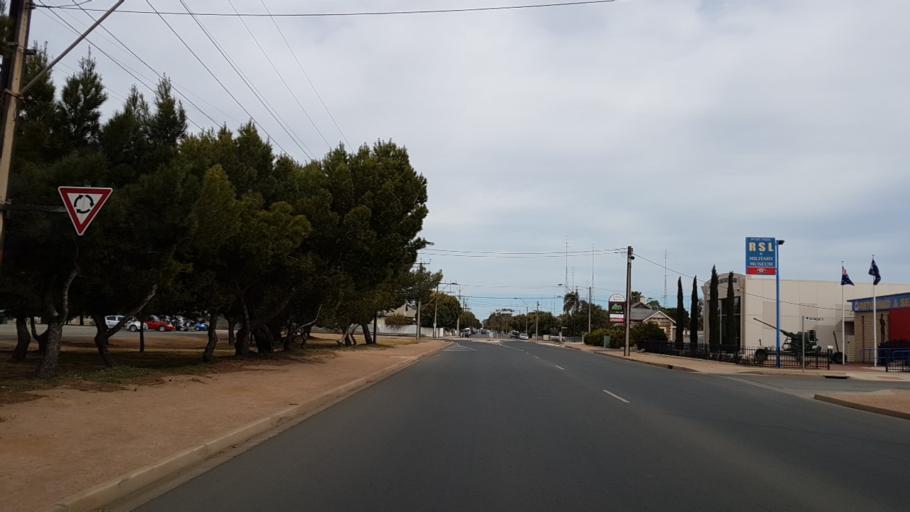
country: AU
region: South Australia
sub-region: Port Pirie City and Dists
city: Port Pirie
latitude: -33.1884
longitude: 138.0039
